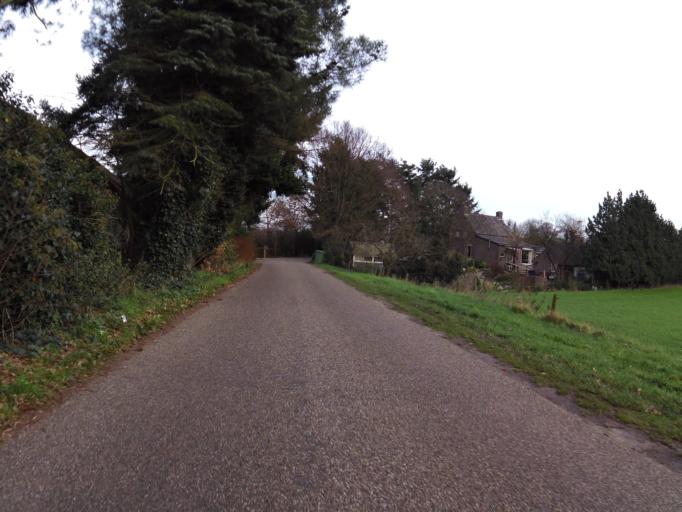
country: NL
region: North Brabant
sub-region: Gemeente Oss
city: Berghem
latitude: 51.7353
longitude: 5.5877
